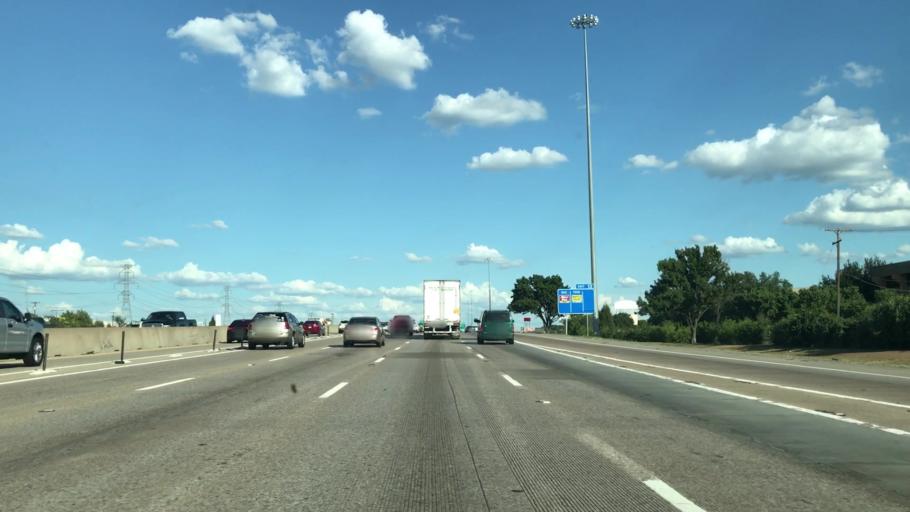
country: US
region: Texas
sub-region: Dallas County
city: Garland
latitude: 32.8832
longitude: -96.6973
